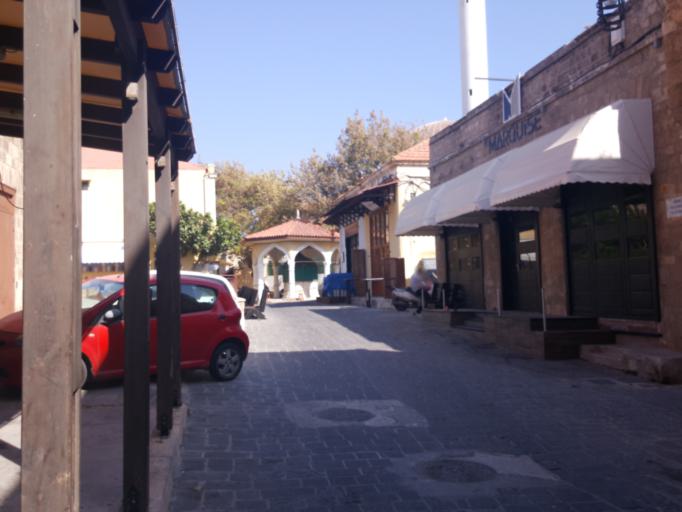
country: GR
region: South Aegean
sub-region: Nomos Dodekanisou
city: Rodos
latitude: 36.4430
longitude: 28.2272
